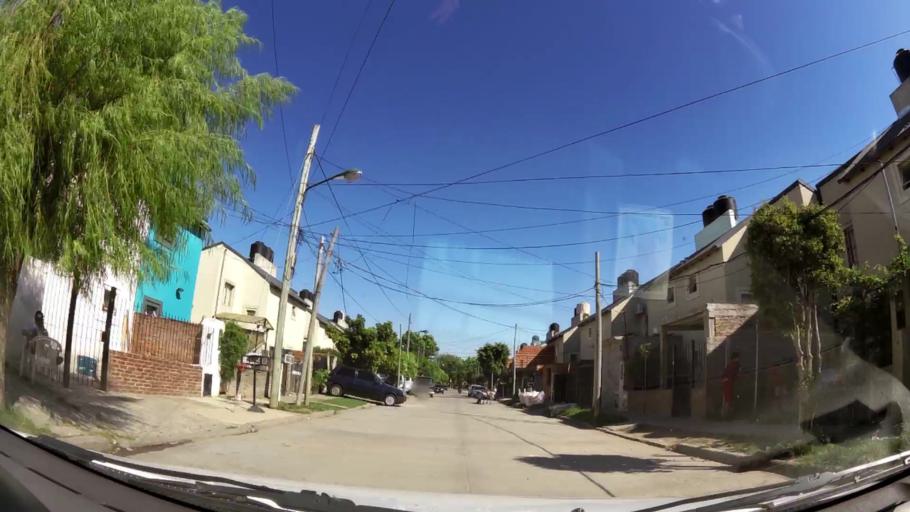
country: AR
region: Buenos Aires
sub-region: Partido de San Isidro
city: San Isidro
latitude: -34.4720
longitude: -58.5394
